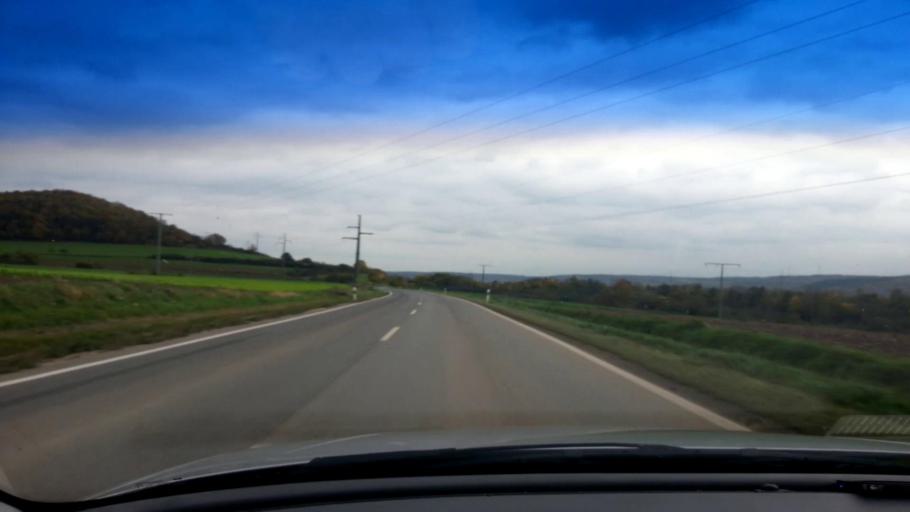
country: DE
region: Bavaria
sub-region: Regierungsbezirk Unterfranken
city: Stettfeld
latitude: 49.9658
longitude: 10.7273
